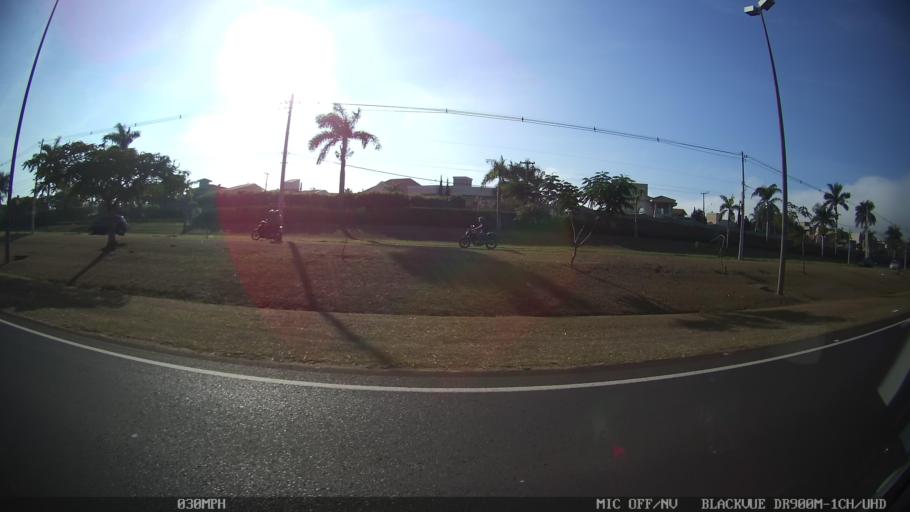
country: BR
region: Sao Paulo
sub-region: Sao Jose Do Rio Preto
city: Sao Jose do Rio Preto
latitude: -20.8149
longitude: -49.3475
